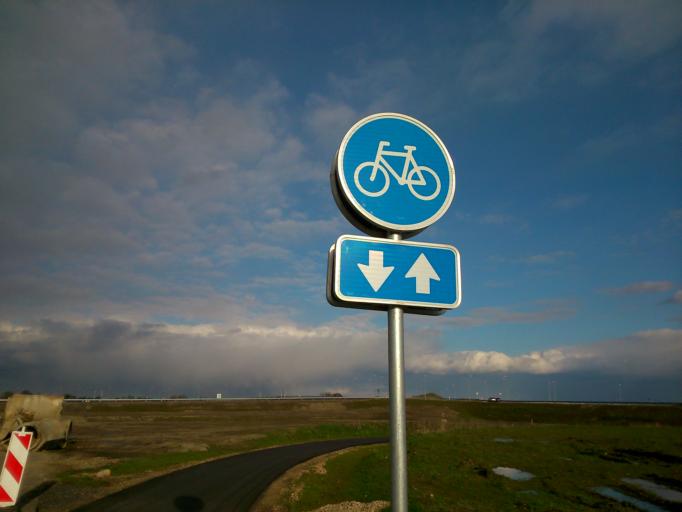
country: DK
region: Central Jutland
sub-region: Herning Kommune
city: Snejbjerg
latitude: 56.1288
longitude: 8.8715
